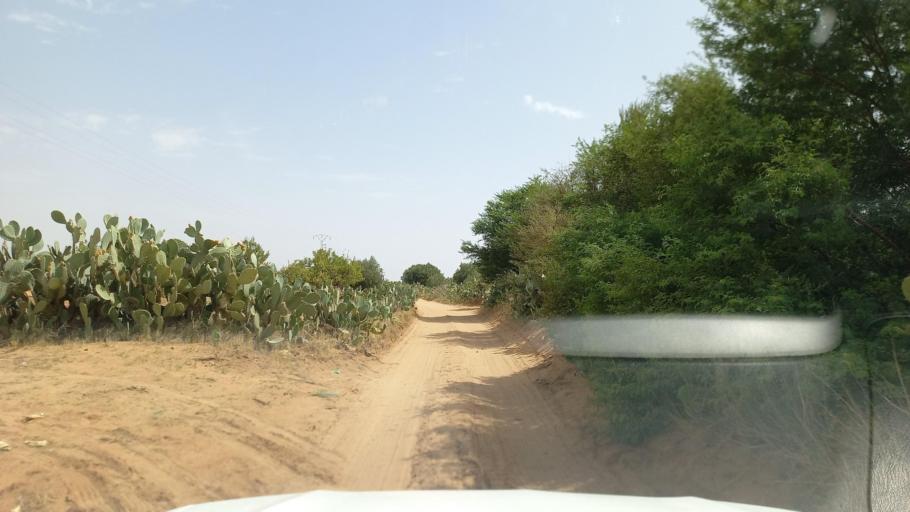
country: TN
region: Al Qasrayn
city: Kasserine
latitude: 35.2604
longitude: 9.0521
